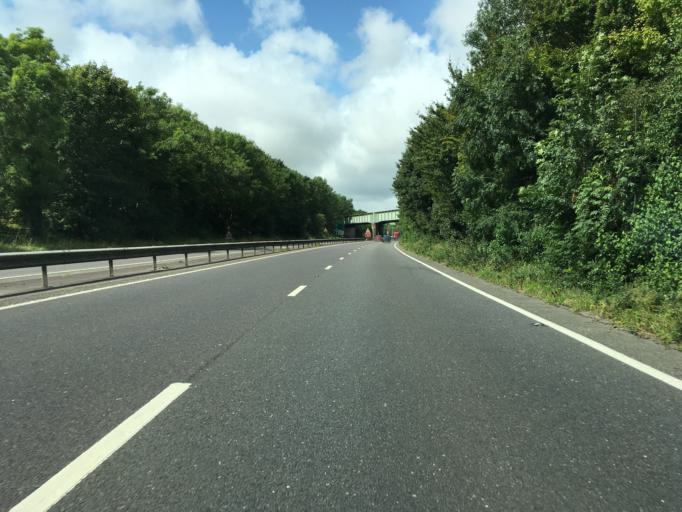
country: GB
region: England
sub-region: East Sussex
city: Lewes
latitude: 50.8669
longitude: -0.0142
